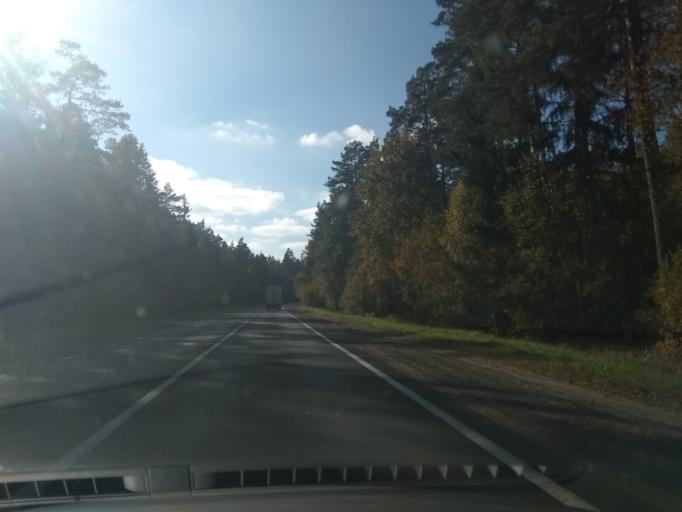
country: BY
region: Brest
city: Baranovichi
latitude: 53.0502
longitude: 25.8551
